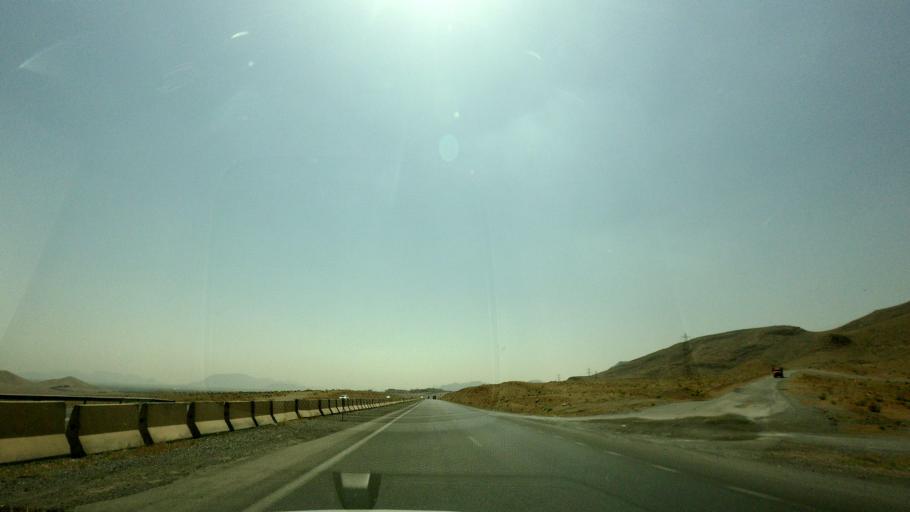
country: IR
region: Isfahan
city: Najafabad
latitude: 32.5392
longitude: 51.3187
